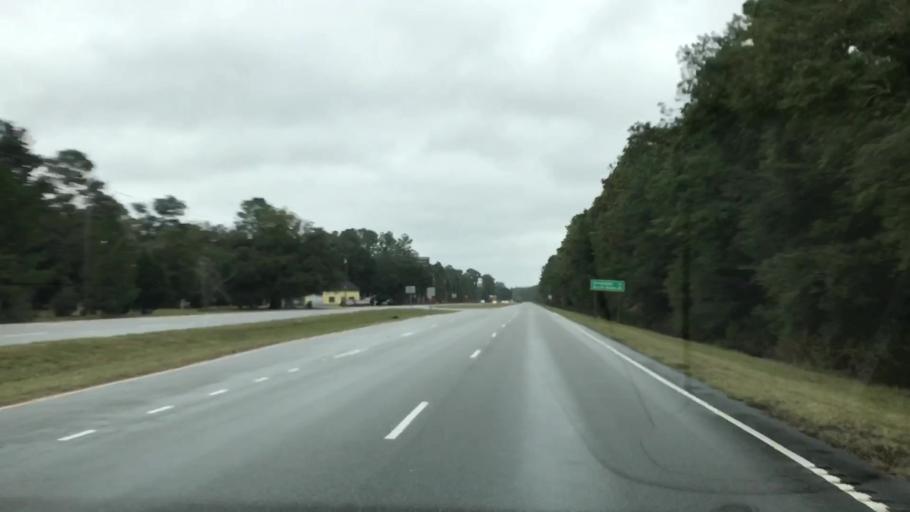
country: US
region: South Carolina
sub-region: Georgetown County
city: Georgetown
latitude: 33.2202
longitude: -79.3791
